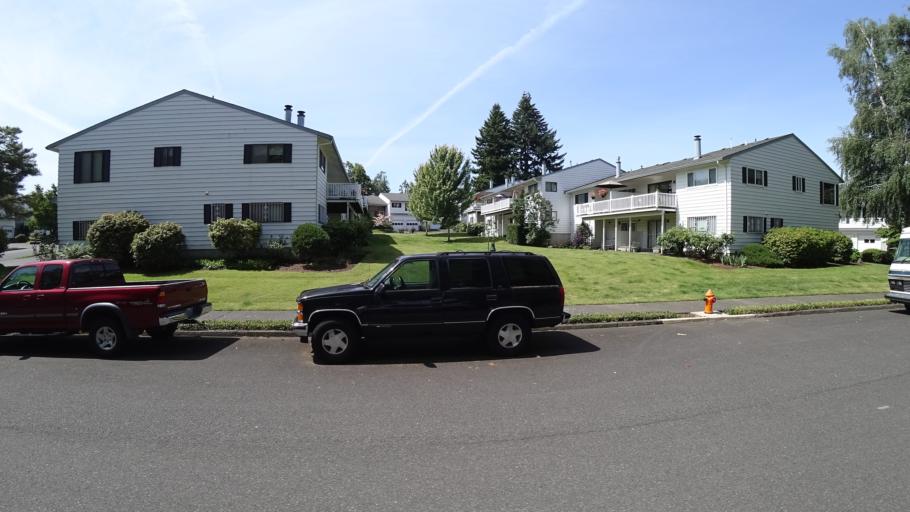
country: US
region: Oregon
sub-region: Multnomah County
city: Fairview
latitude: 45.5445
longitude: -122.5070
